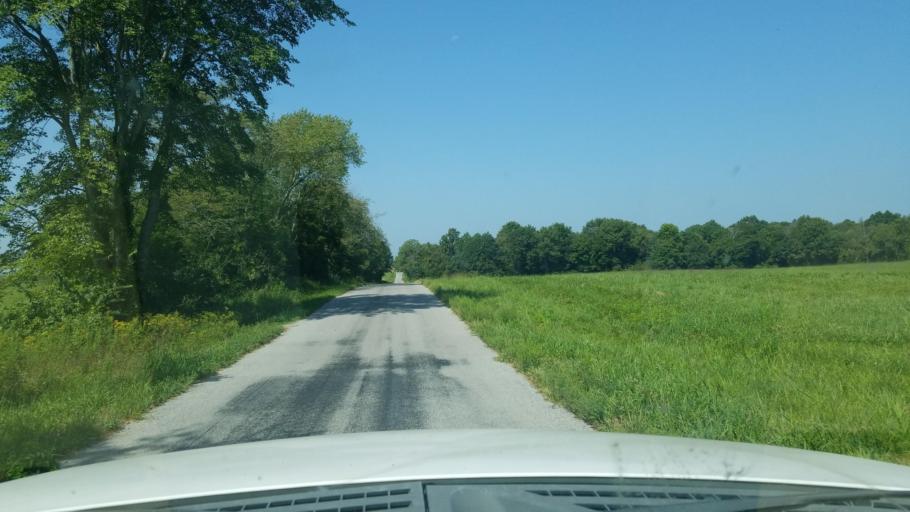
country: US
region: Illinois
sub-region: Saline County
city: Harrisburg
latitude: 37.8922
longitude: -88.6618
